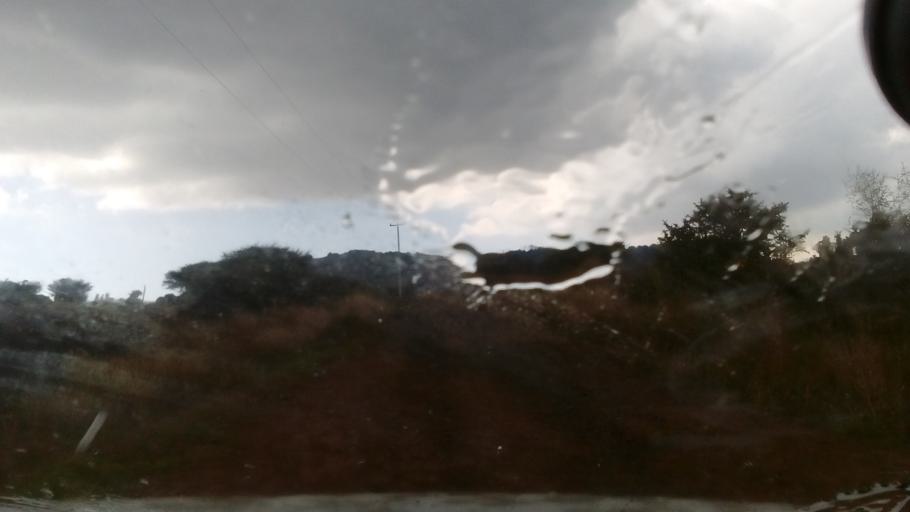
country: MX
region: Guanajuato
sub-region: Silao de la Victoria
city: San Francisco (Banos de Agua Caliente)
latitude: 21.1593
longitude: -101.4252
